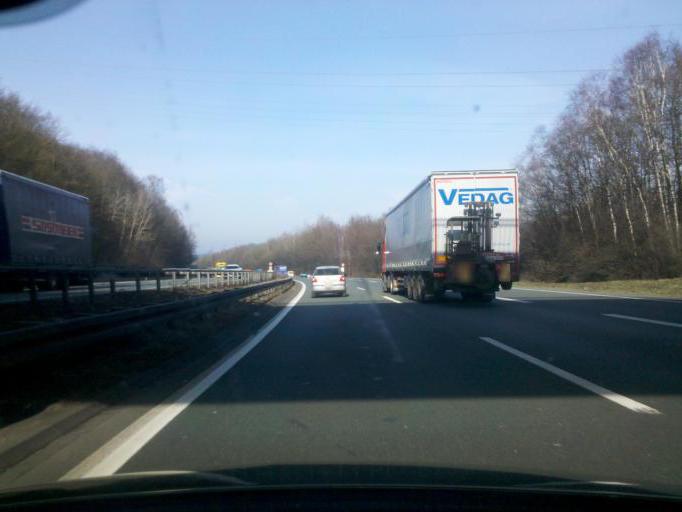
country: DE
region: North Rhine-Westphalia
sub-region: Regierungsbezirk Arnsberg
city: Wilnsdorf
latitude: 50.8173
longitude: 8.0918
